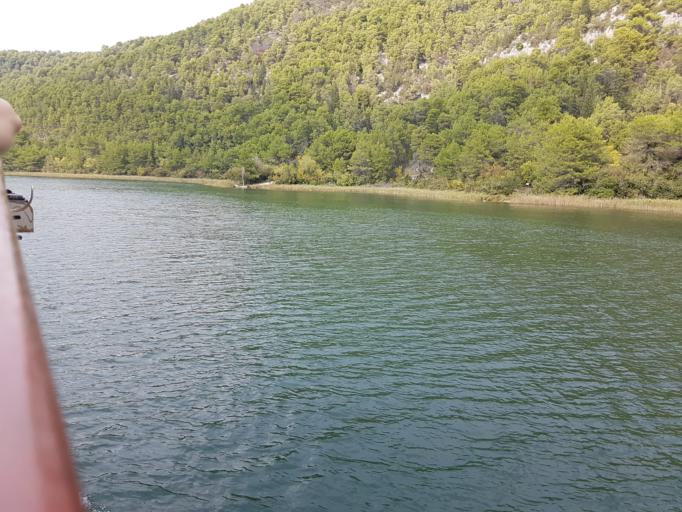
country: HR
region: Sibensko-Kniniska
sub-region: Grad Sibenik
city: Sibenik
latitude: 43.8187
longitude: 15.9488
